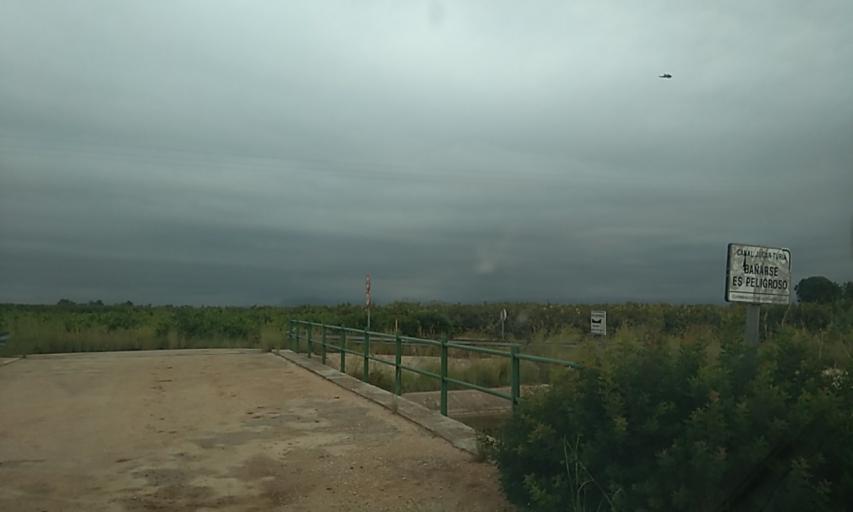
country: ES
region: Valencia
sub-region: Provincia de Valencia
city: Benimodo
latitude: 39.1931
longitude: -0.5678
